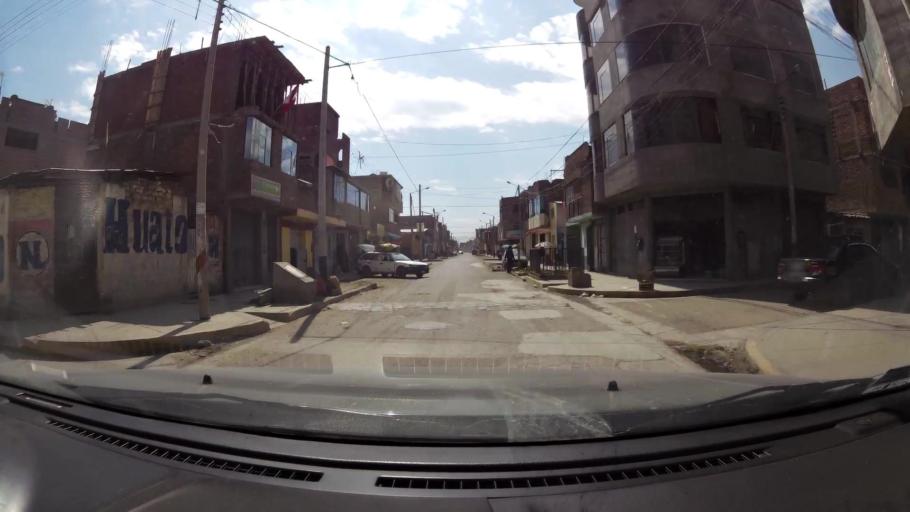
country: PE
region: Junin
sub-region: Provincia de Huancayo
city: Huancayo
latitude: -12.0883
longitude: -75.2040
